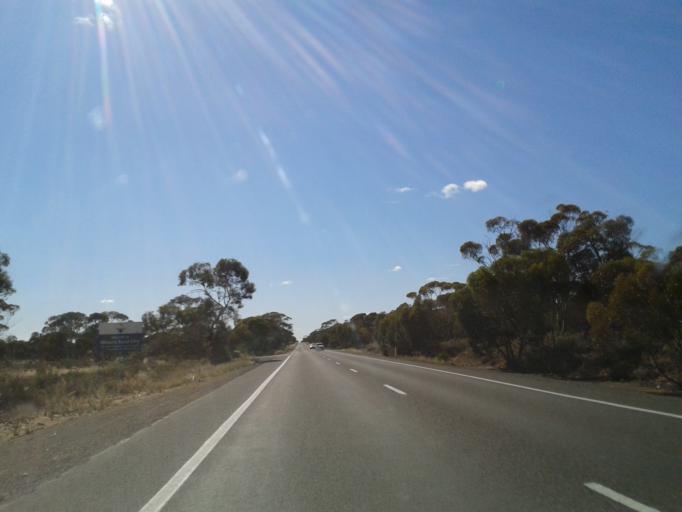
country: AU
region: South Australia
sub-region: Renmark Paringa
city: Renmark
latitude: -34.2742
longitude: 140.9645
